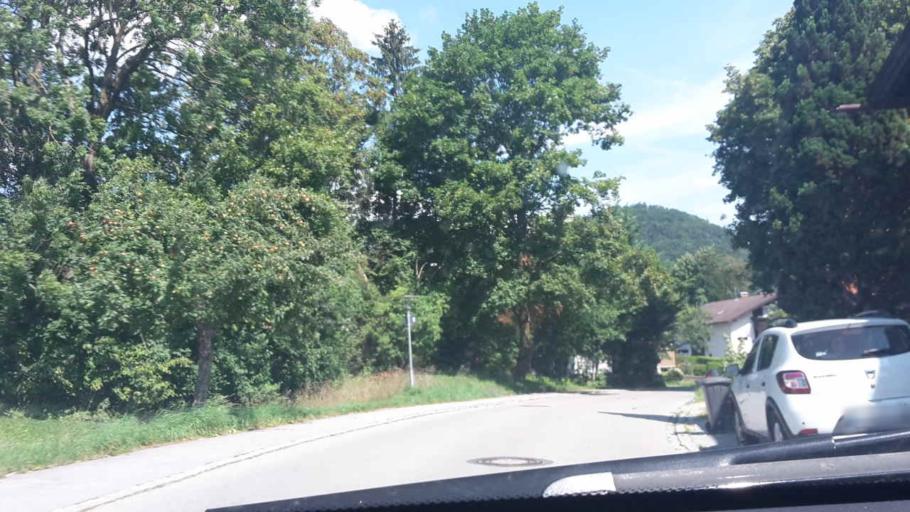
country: DE
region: Bavaria
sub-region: Upper Bavaria
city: Oberaudorf
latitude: 47.6618
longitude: 12.1743
